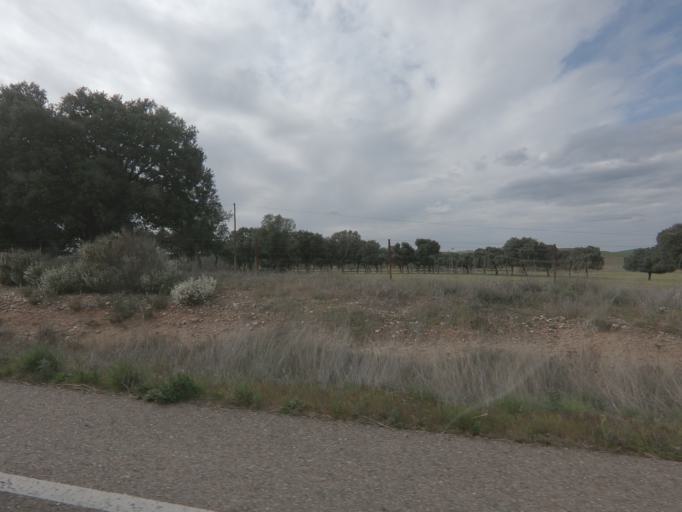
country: ES
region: Castille and Leon
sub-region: Provincia de Salamanca
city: Ciudad Rodrigo
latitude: 40.5651
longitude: -6.5498
